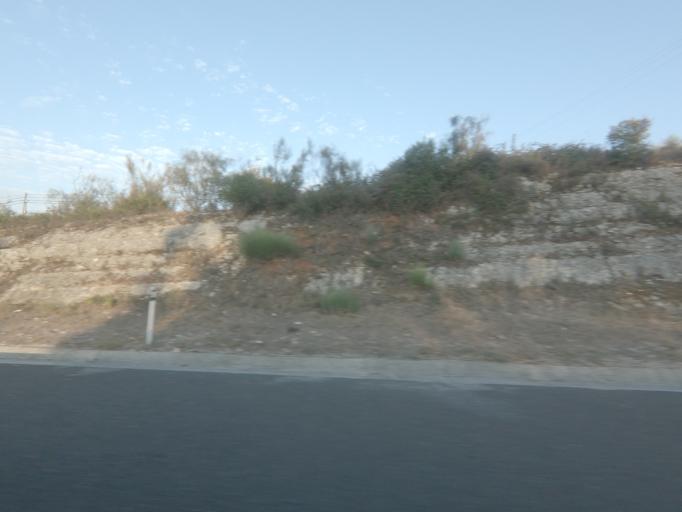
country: PT
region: Leiria
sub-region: Leiria
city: Santa Catarina da Serra
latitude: 39.6684
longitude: -8.6869
